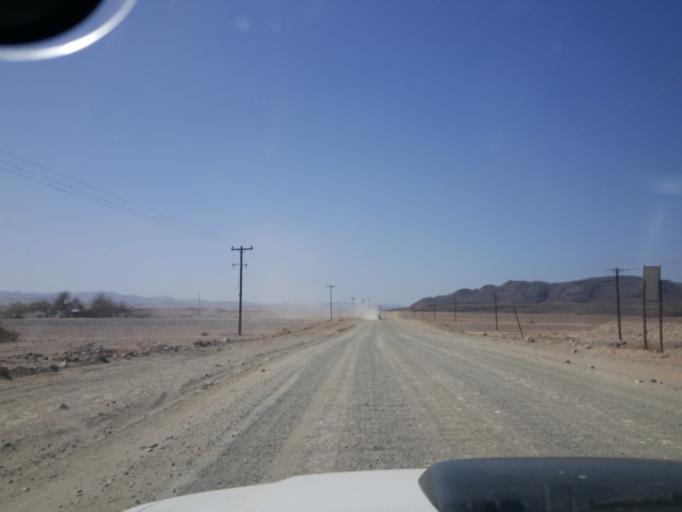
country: ZA
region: Northern Cape
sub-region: Namakwa District Municipality
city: Port Nolloth
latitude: -28.6992
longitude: 17.5913
